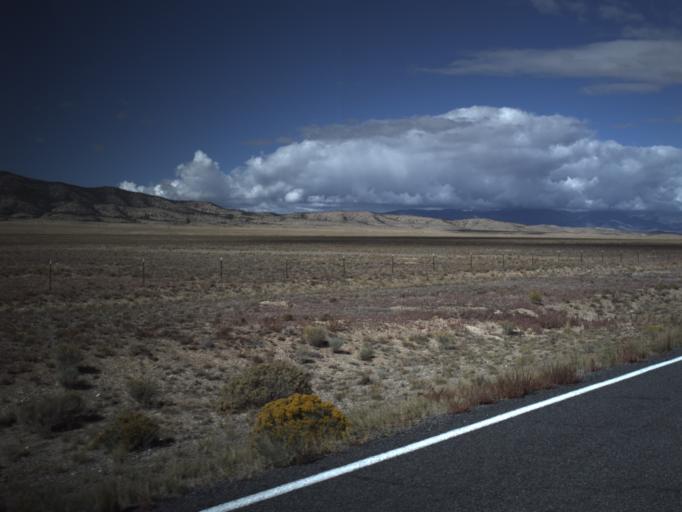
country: US
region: Utah
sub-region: Beaver County
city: Milford
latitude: 38.6505
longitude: -113.8691
